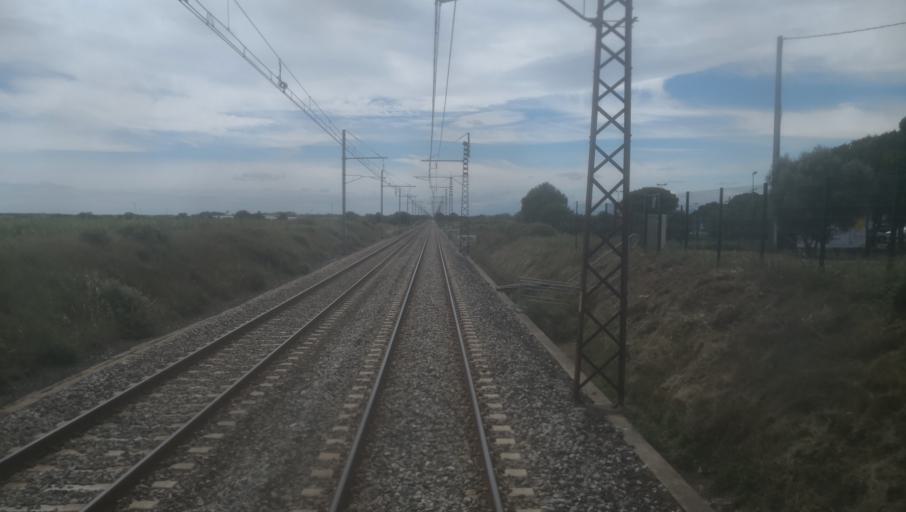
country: FR
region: Languedoc-Roussillon
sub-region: Departement de l'Herault
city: Portiragnes
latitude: 43.3198
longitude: 3.3547
